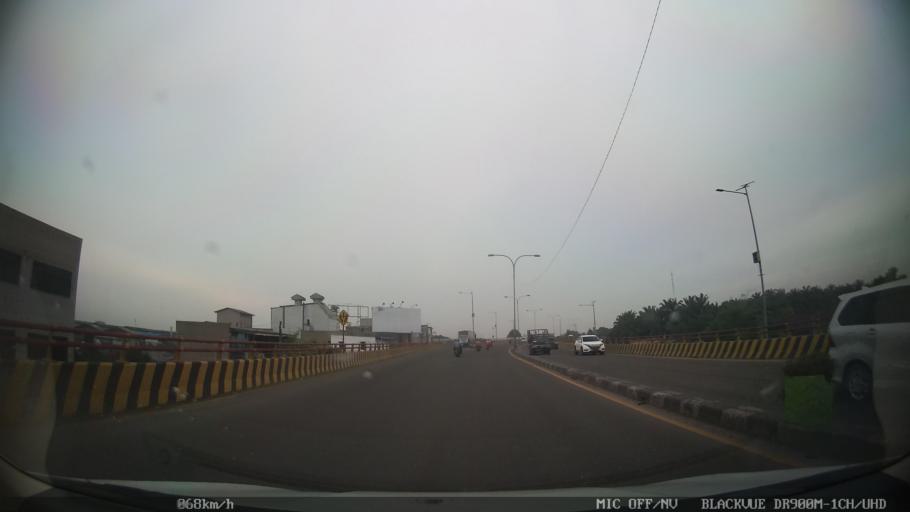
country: ID
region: North Sumatra
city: Deli Tua
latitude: 3.5363
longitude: 98.7183
